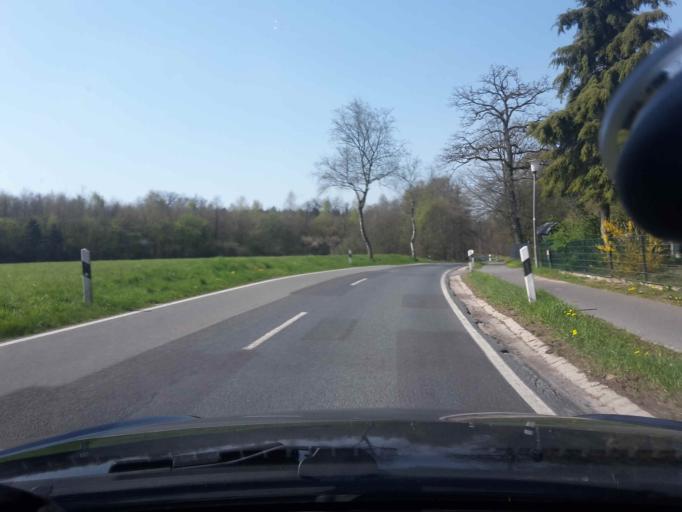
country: DE
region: Lower Saxony
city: Handeloh
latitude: 53.2544
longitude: 9.8827
